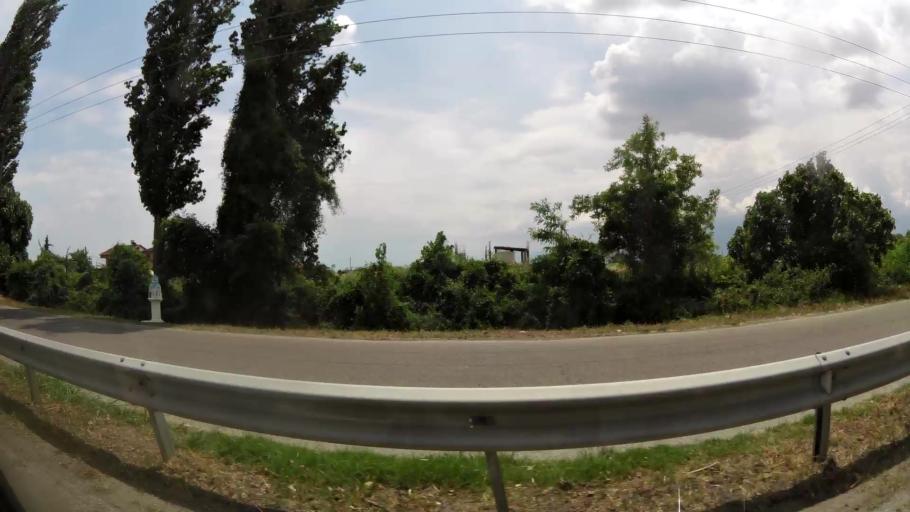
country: GR
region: Central Macedonia
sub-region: Nomos Pierias
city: Peristasi
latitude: 40.2725
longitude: 22.5554
